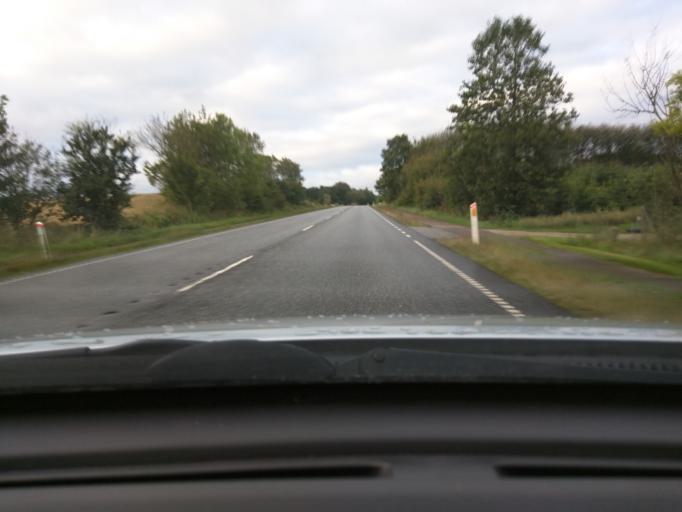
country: DK
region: Central Jutland
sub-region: Silkeborg Kommune
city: Kjellerup
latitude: 56.3401
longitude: 9.3467
